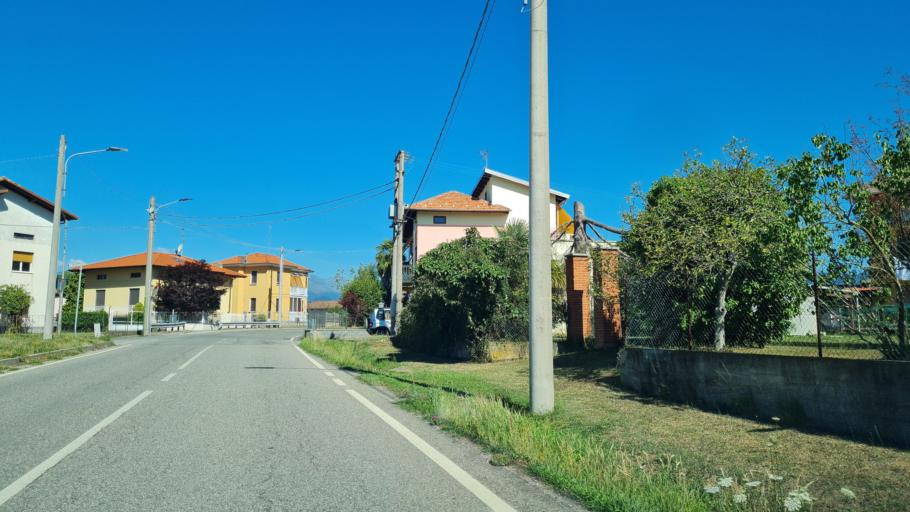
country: IT
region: Piedmont
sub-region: Provincia di Biella
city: Cossato
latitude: 45.5624
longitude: 8.1973
